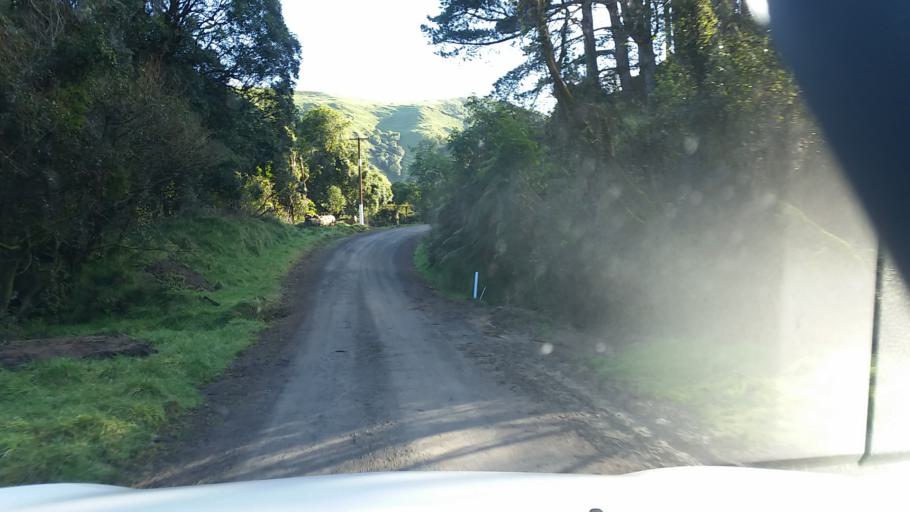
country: NZ
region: Taranaki
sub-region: South Taranaki District
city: Eltham
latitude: -39.5093
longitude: 174.3974
